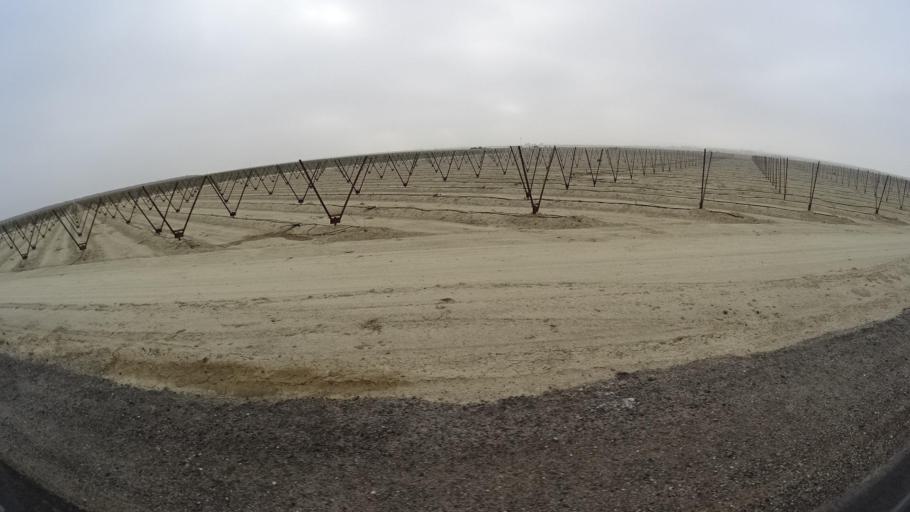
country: US
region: California
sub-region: Kern County
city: Maricopa
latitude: 35.1169
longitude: -119.3554
